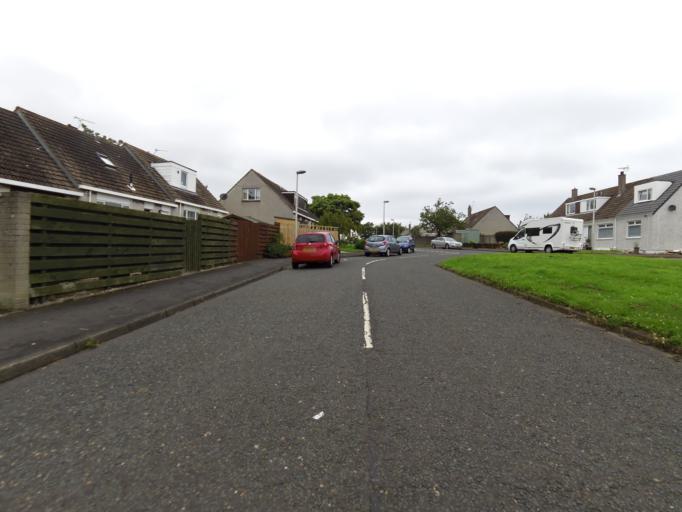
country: GB
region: Scotland
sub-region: East Lothian
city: Musselburgh
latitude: 55.9327
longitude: -3.0674
